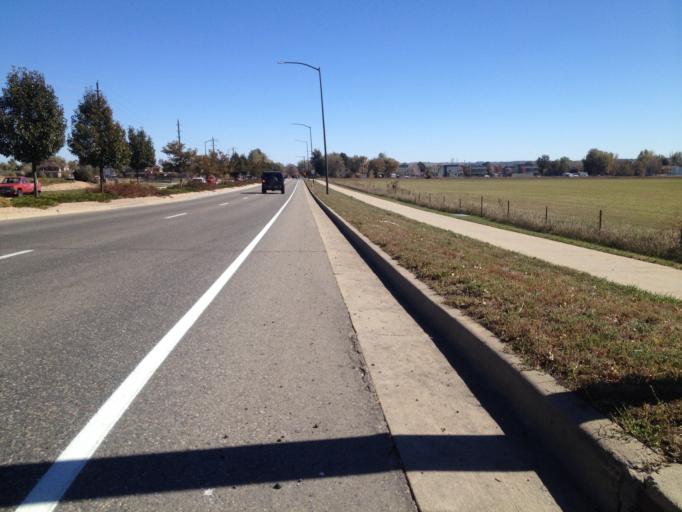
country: US
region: Colorado
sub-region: Boulder County
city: Louisville
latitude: 39.9868
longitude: -105.1231
